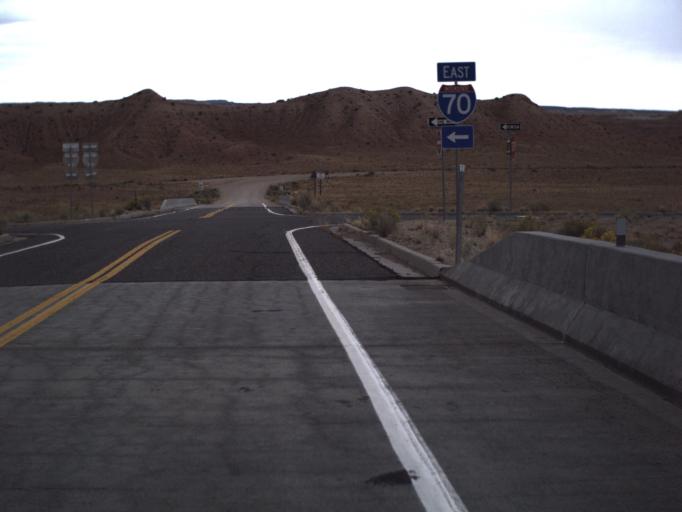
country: US
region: Utah
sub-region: Emery County
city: Ferron
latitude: 38.8421
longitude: -111.0643
